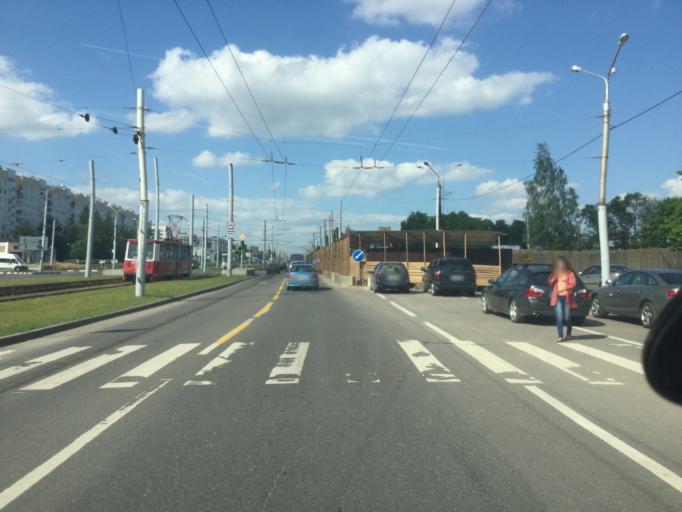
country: BY
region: Vitebsk
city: Vitebsk
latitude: 55.1672
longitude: 30.2414
